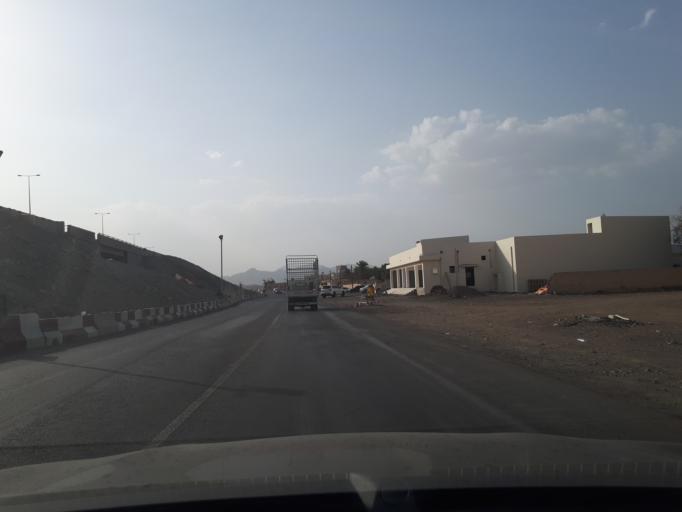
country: OM
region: Ash Sharqiyah
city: Ibra'
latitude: 22.8316
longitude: 58.4271
